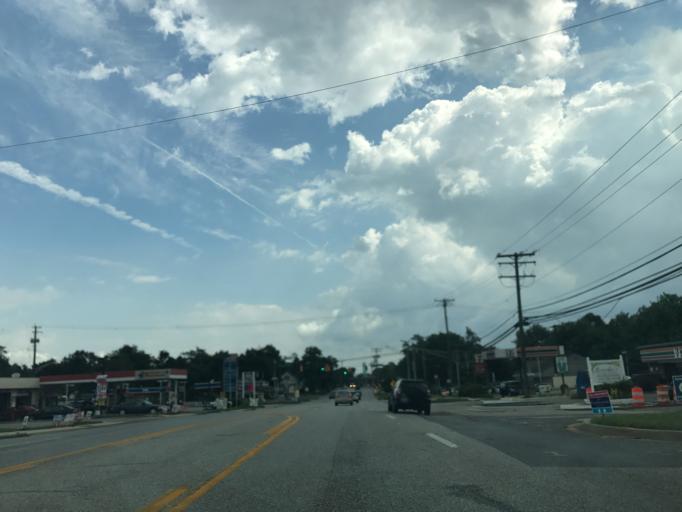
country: US
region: Maryland
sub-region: Anne Arundel County
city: Glen Burnie
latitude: 39.1480
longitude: -76.6392
